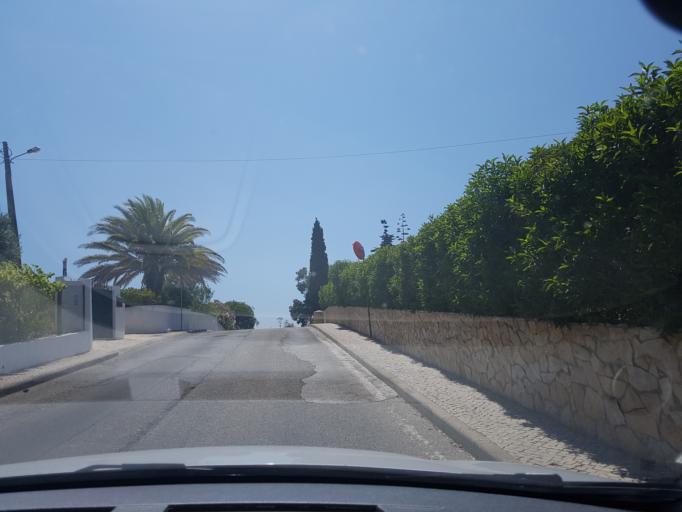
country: PT
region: Faro
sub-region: Lagoa
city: Carvoeiro
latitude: 37.1004
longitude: -8.4560
